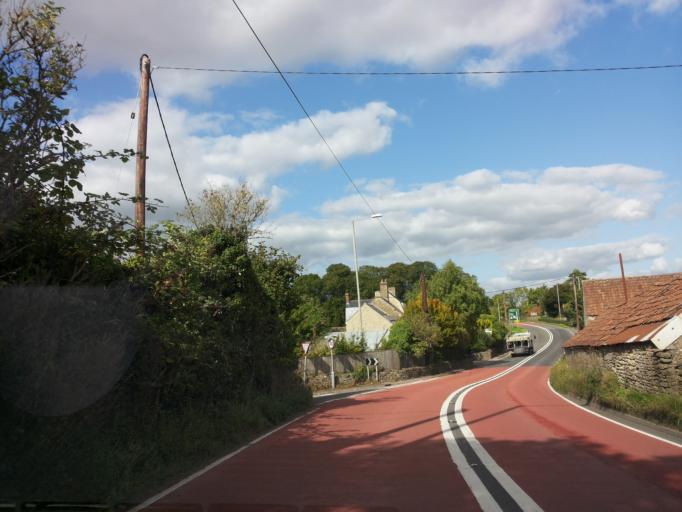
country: GB
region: England
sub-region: Bath and North East Somerset
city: Hinton Charterhouse
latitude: 51.2837
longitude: -2.3008
